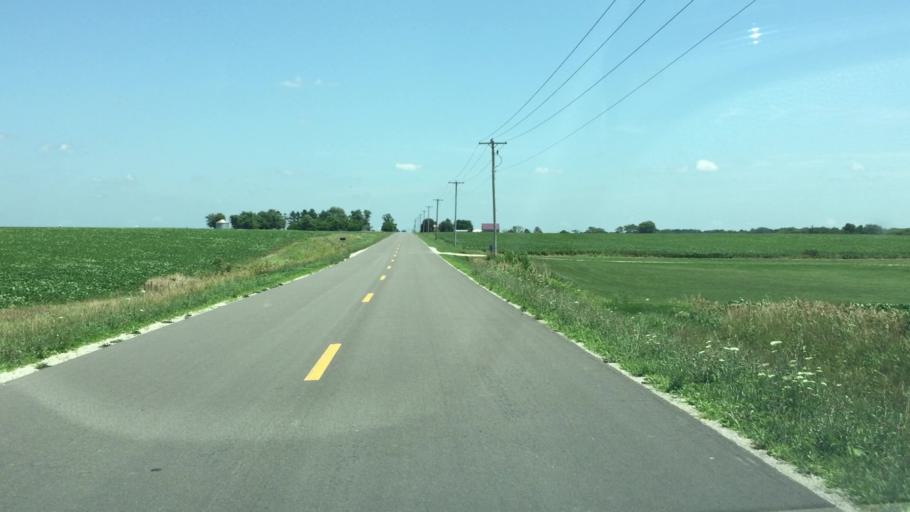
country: US
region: Illinois
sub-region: Hancock County
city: Carthage
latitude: 40.3280
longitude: -91.1791
